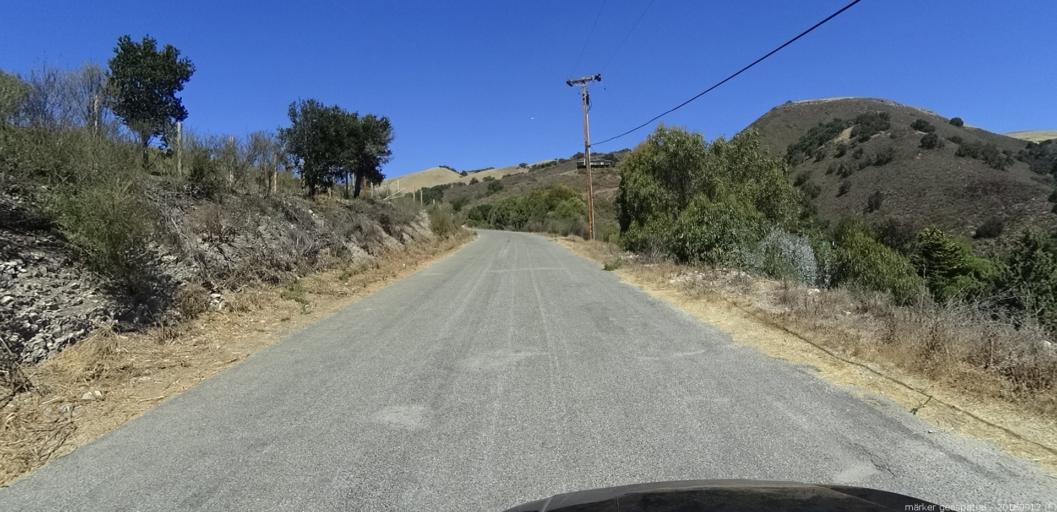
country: US
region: California
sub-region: Monterey County
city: Carmel Valley Village
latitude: 36.4913
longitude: -121.7185
